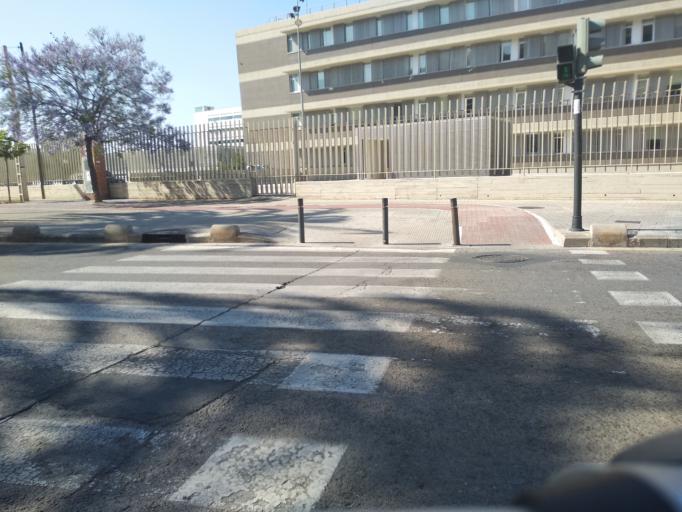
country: ES
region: Valencia
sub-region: Provincia de Valencia
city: Alboraya
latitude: 39.4782
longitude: -0.3464
